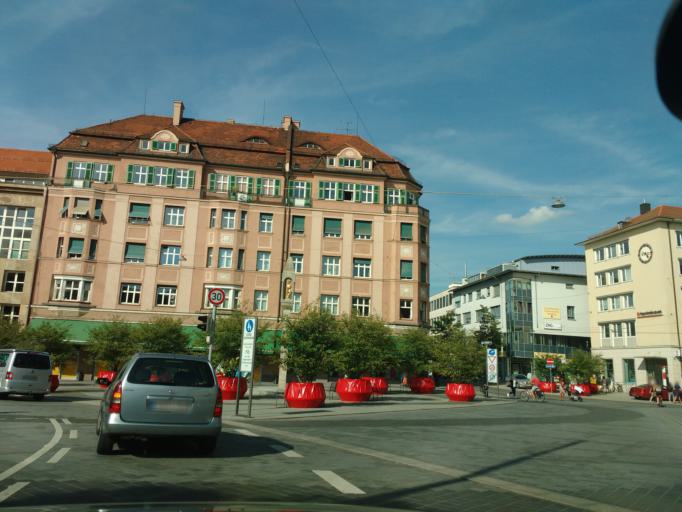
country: DE
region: Bavaria
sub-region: Upper Bavaria
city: Pasing
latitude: 48.1464
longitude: 11.4593
